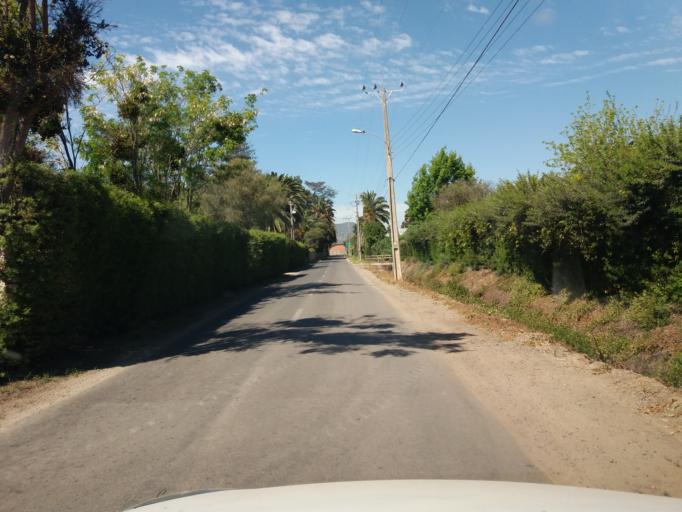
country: CL
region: Valparaiso
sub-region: Provincia de Quillota
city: Quillota
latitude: -32.8746
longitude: -71.2197
